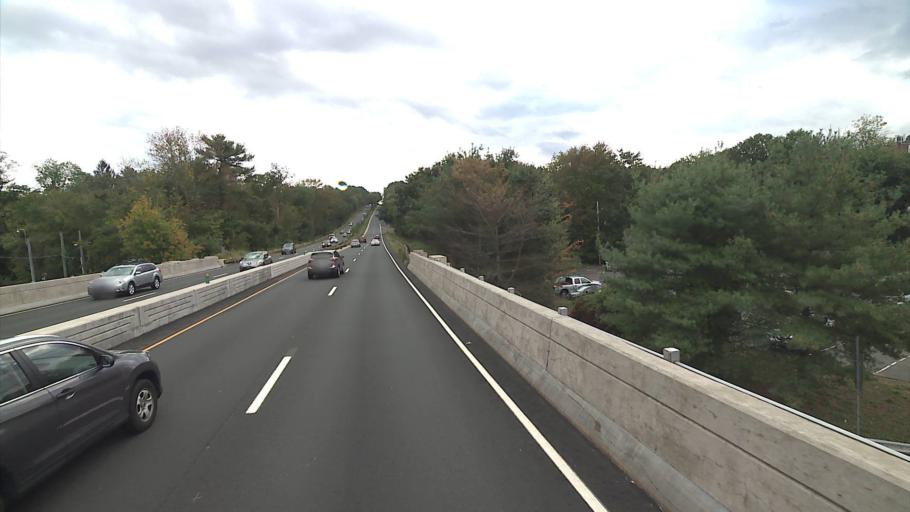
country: US
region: Connecticut
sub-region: Fairfield County
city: North Stamford
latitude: 41.1119
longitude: -73.5466
